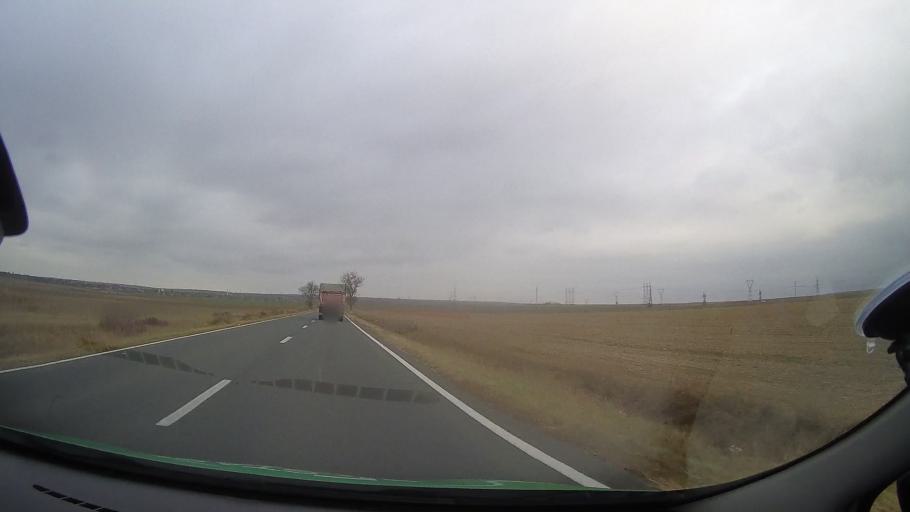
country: RO
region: Constanta
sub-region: Comuna Castelu
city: Castelu
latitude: 44.2520
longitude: 28.3551
